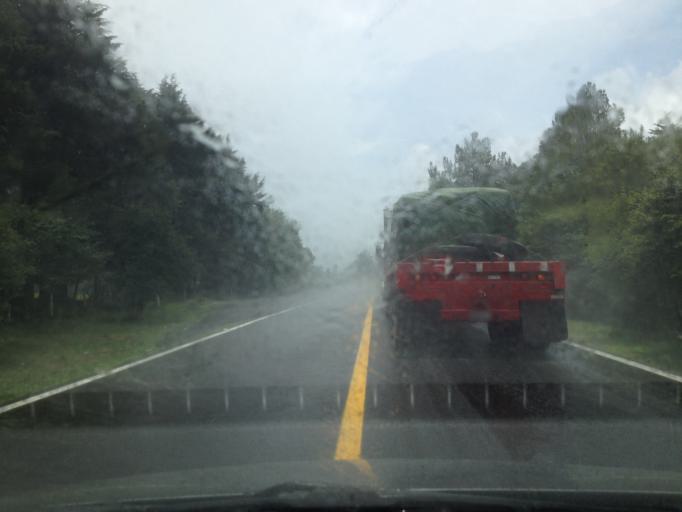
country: MX
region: Michoacan
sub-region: Patzcuaro
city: Santa Maria Huiramangaro (San Juan Tumbio)
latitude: 19.4900
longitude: -101.7957
